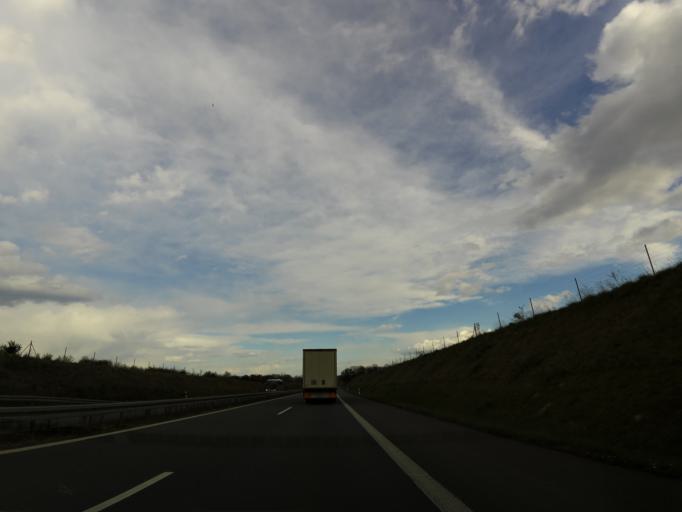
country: DE
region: Saxony-Anhalt
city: Quedlinburg
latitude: 51.8127
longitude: 11.1719
